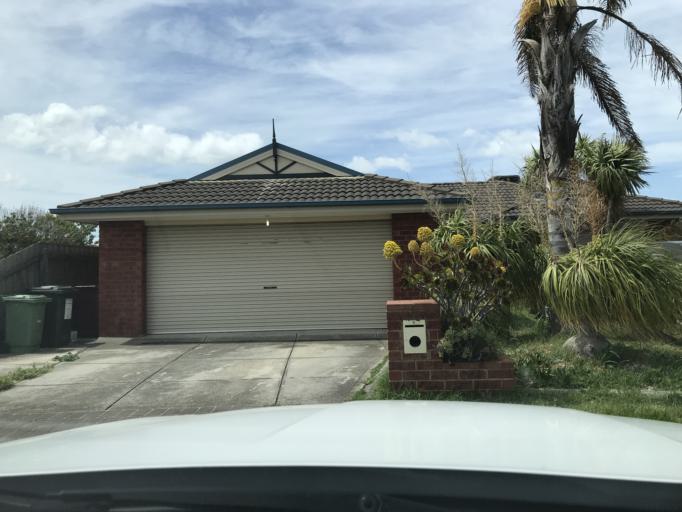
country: AU
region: Victoria
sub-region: Hume
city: Roxburgh Park
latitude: -37.6133
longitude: 144.9369
